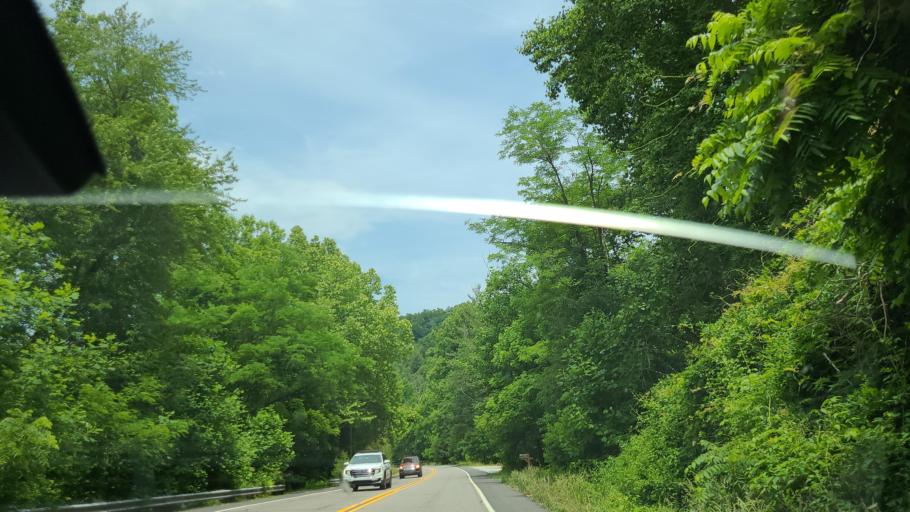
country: US
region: North Carolina
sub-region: Macon County
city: Franklin
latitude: 35.1403
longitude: -83.2863
